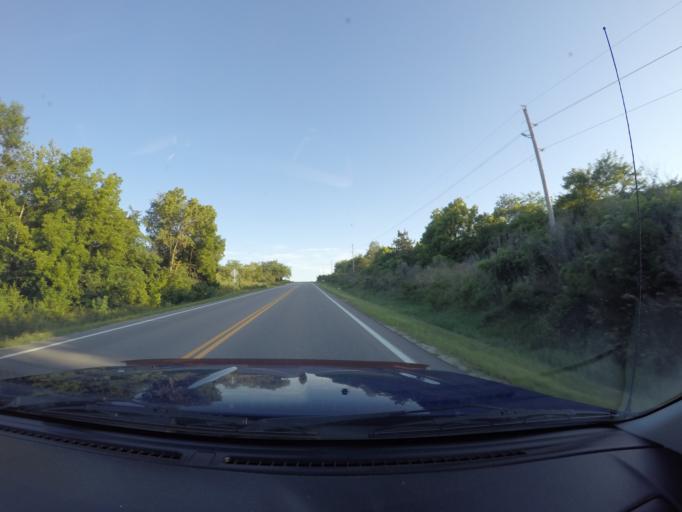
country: US
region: Kansas
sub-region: Pottawatomie County
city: Wamego
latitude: 39.1147
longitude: -96.2893
